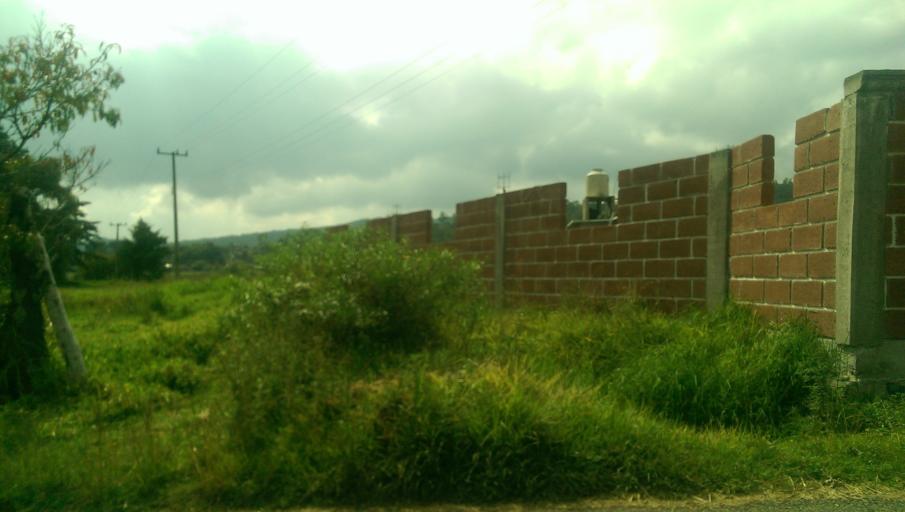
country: MX
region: Mexico
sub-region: Jilotepec
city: Jilotepec de Molina Enriquez
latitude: 19.9496
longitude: -99.4880
